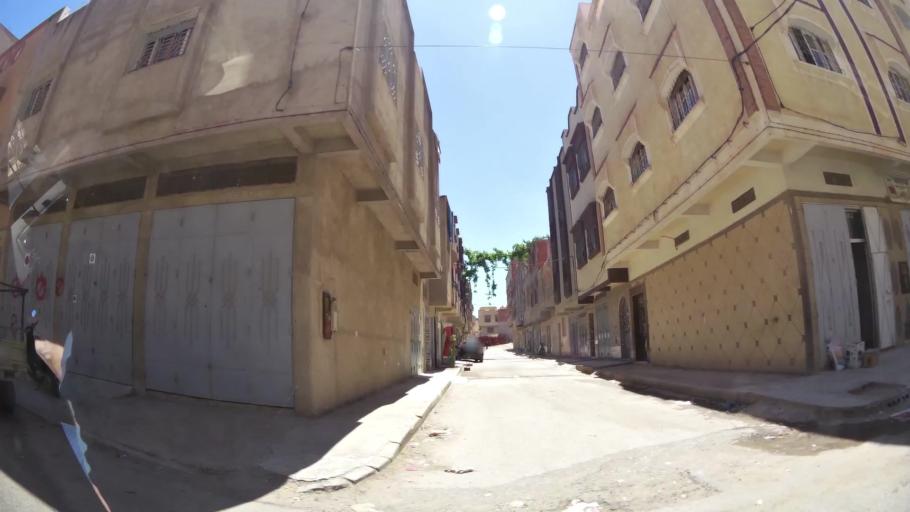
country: MA
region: Oriental
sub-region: Oujda-Angad
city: Oujda
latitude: 34.6604
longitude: -1.9255
